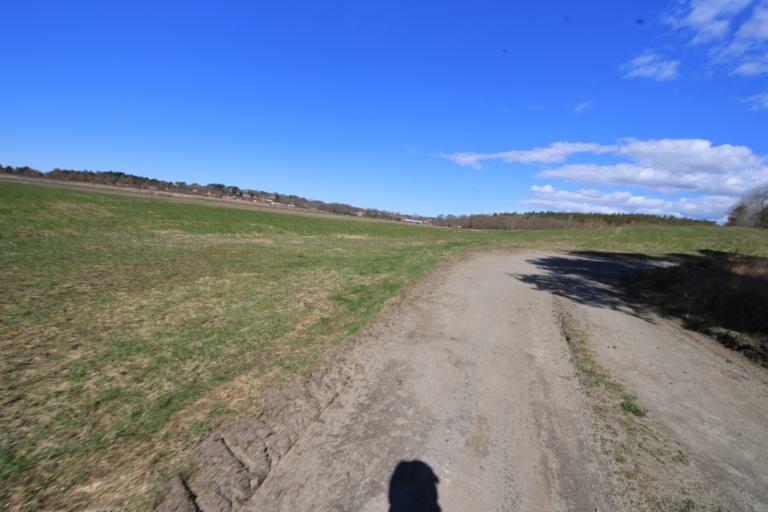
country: SE
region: Halland
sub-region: Varbergs Kommun
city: Varberg
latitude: 57.1840
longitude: 12.2298
